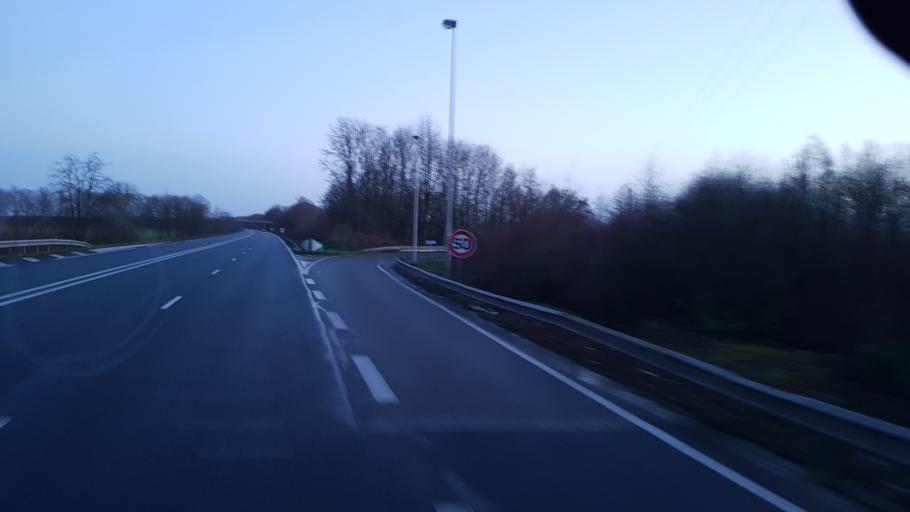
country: FR
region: Nord-Pas-de-Calais
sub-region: Departement du Nord
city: Ferin
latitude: 50.3353
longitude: 3.0900
